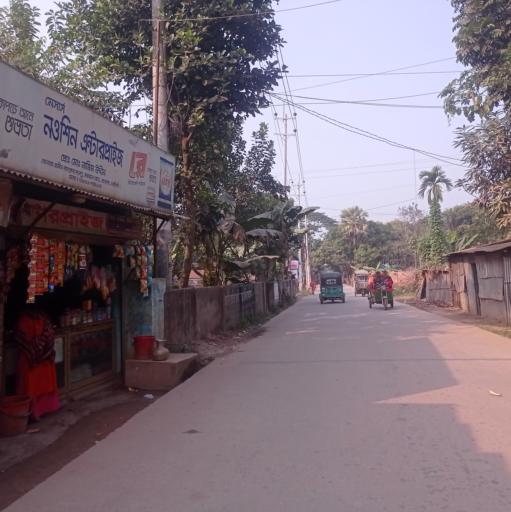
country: BD
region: Dhaka
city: Bhairab Bazar
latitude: 24.0984
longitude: 90.8528
